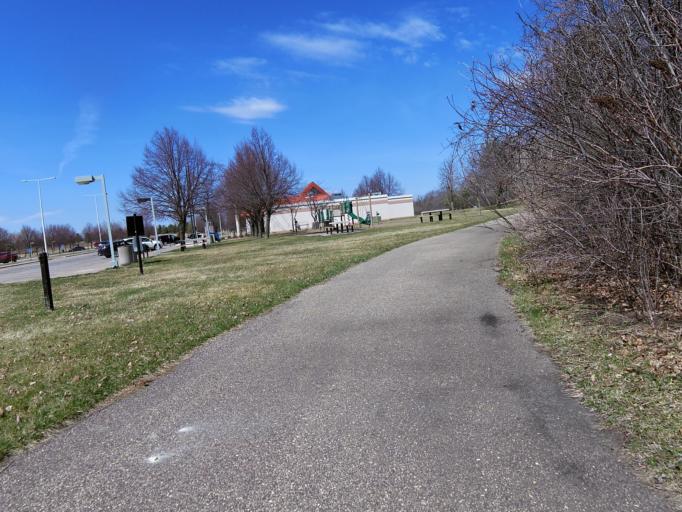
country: US
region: Minnesota
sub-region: Washington County
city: Lakeland
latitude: 44.9507
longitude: -92.8199
